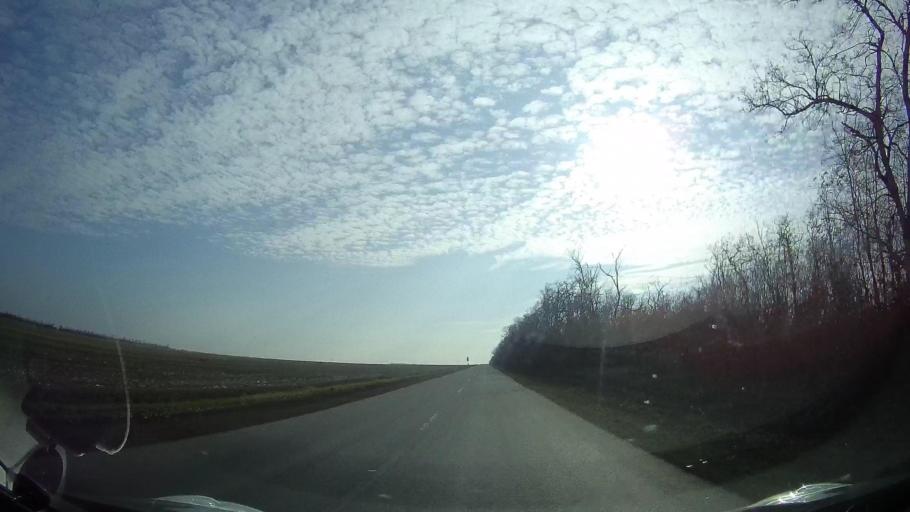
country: RU
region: Rostov
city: Veselyy
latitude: 46.9920
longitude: 40.7200
